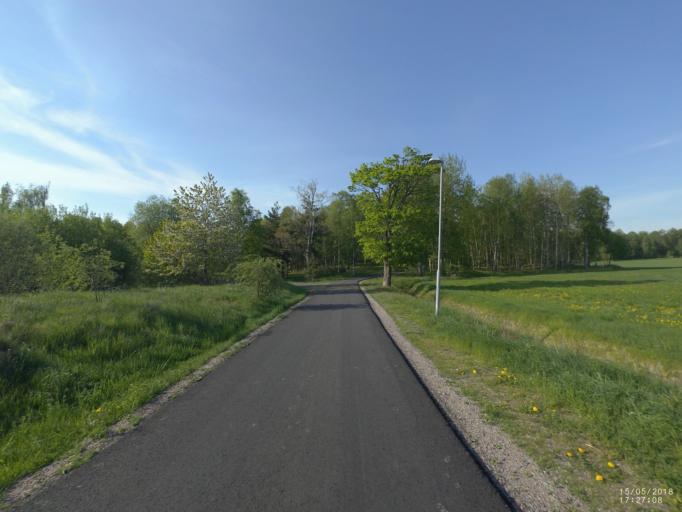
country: SE
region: Soedermanland
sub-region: Nykopings Kommun
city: Nykoping
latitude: 58.7237
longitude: 17.0246
